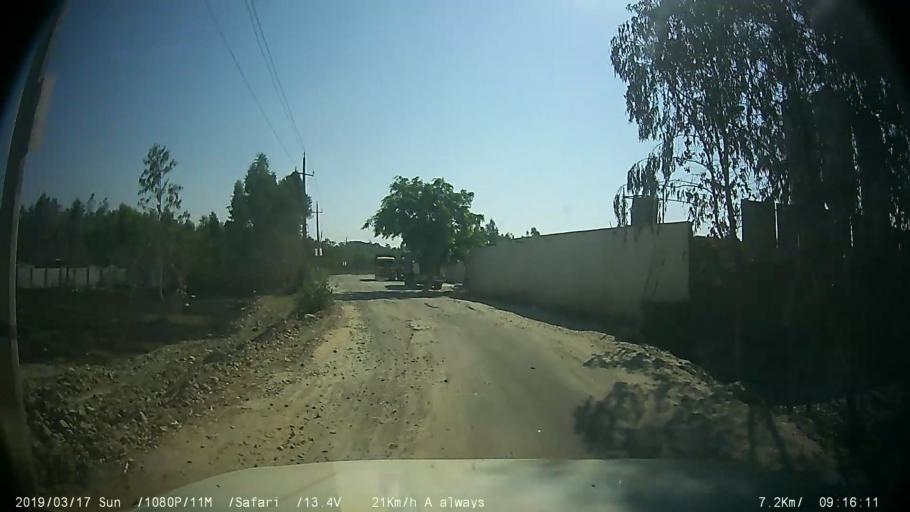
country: IN
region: Karnataka
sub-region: Bangalore Urban
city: Anekal
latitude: 12.8142
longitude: 77.6312
